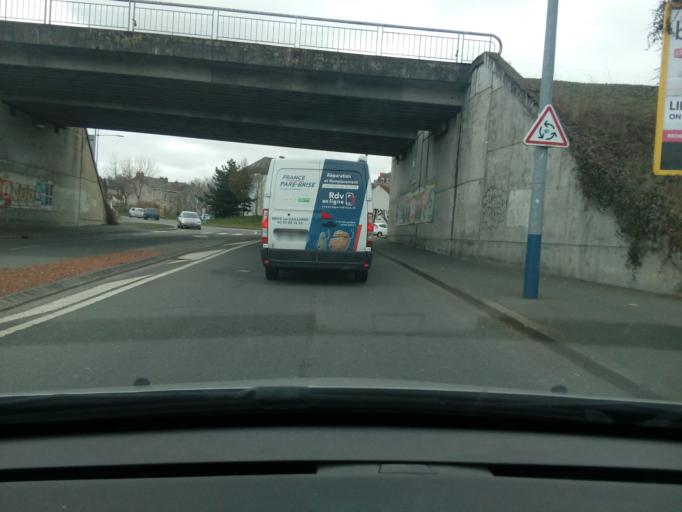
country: FR
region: Limousin
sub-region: Departement de la Creuse
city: Gueret
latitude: 46.1752
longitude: 1.8721
